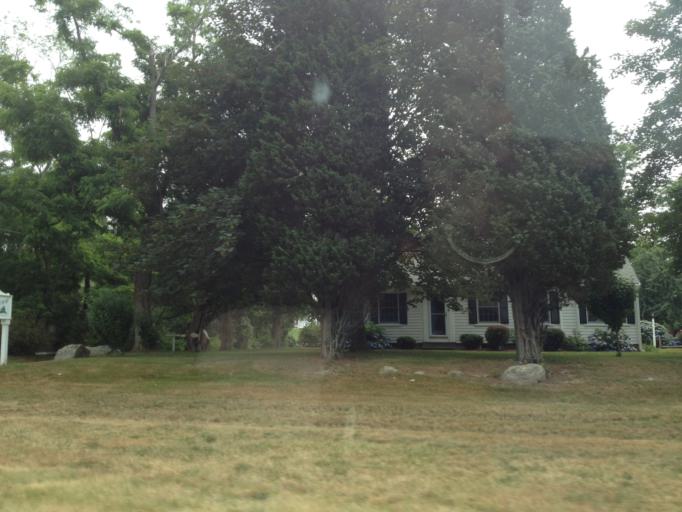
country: US
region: Massachusetts
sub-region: Barnstable County
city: Eastham
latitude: 41.8123
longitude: -69.9703
